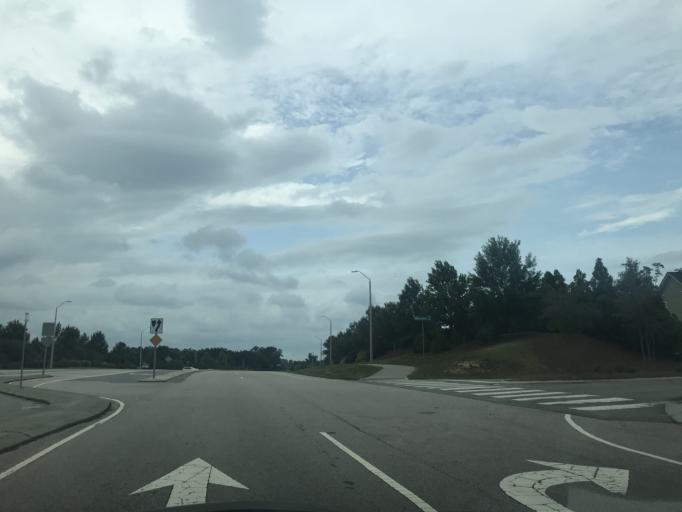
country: US
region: North Carolina
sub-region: Wake County
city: Green Level
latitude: 35.8012
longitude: -78.9013
